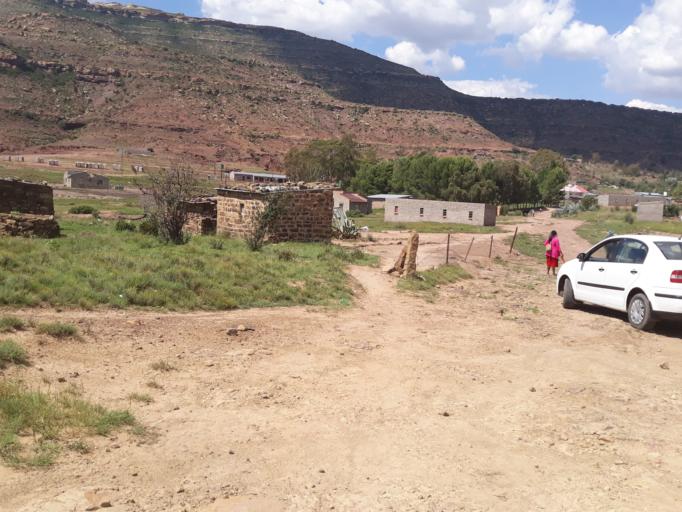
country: LS
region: Quthing
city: Quthing
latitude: -30.3399
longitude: 27.5345
